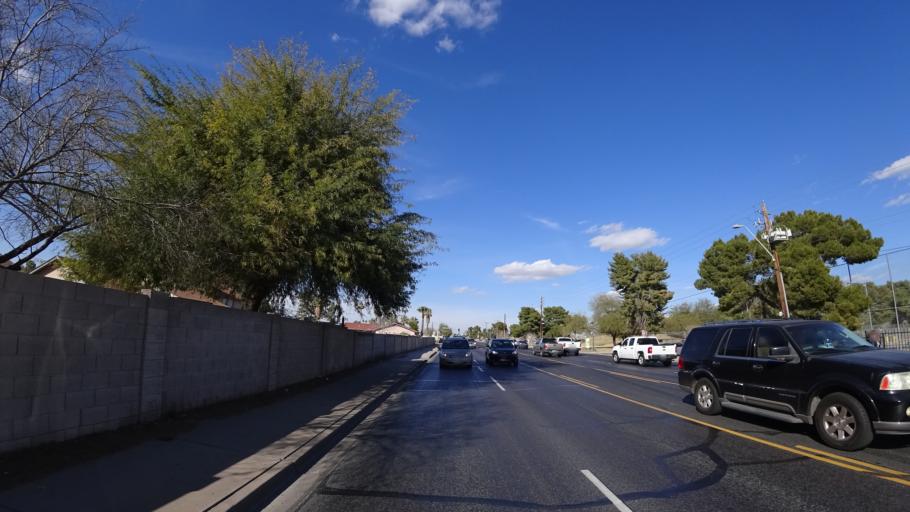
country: US
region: Arizona
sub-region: Maricopa County
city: Tolleson
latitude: 33.4857
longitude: -112.2207
